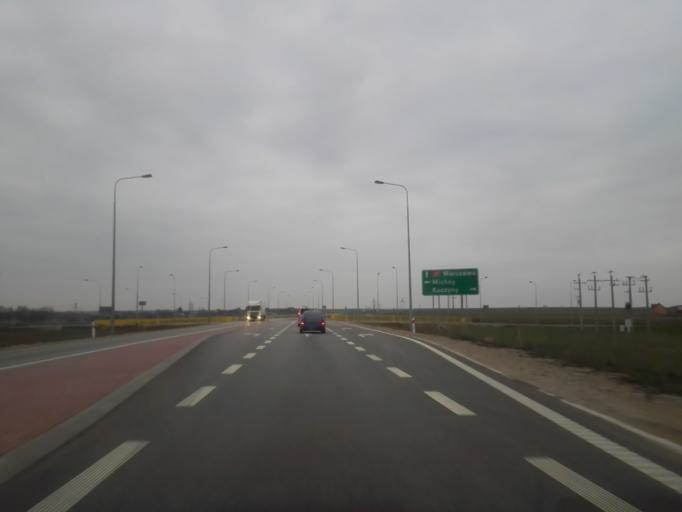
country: PL
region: Podlasie
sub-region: Powiat kolnenski
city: Stawiski
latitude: 53.4035
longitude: 22.1582
